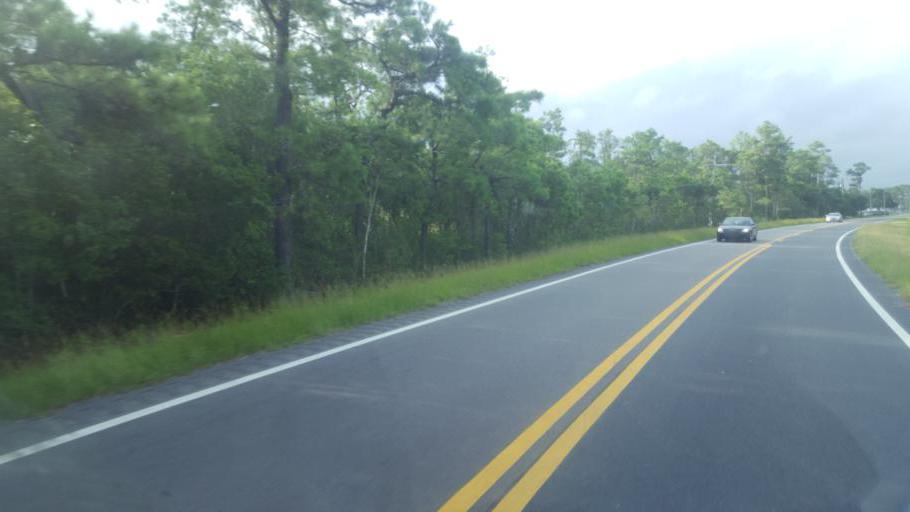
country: US
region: North Carolina
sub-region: Dare County
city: Manteo
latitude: 35.8862
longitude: -75.6586
